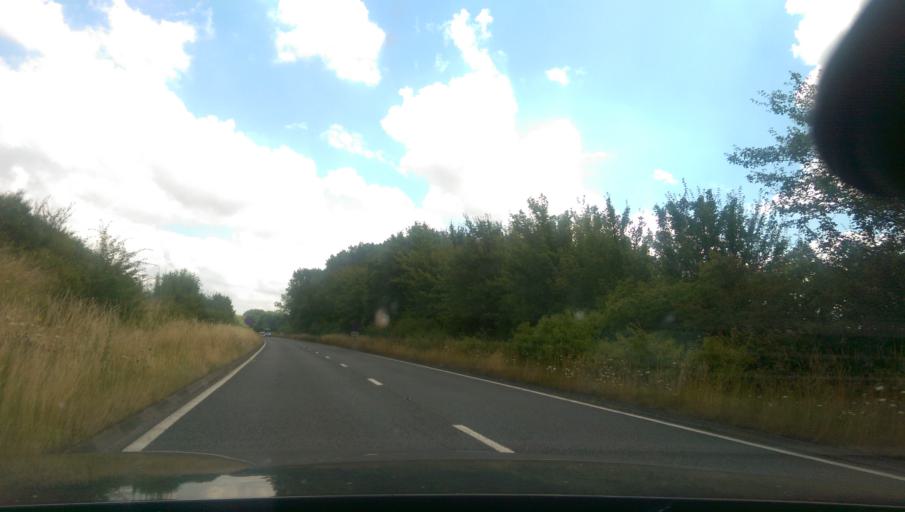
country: GB
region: England
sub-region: Wiltshire
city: Stapleford
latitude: 51.1328
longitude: -1.9214
